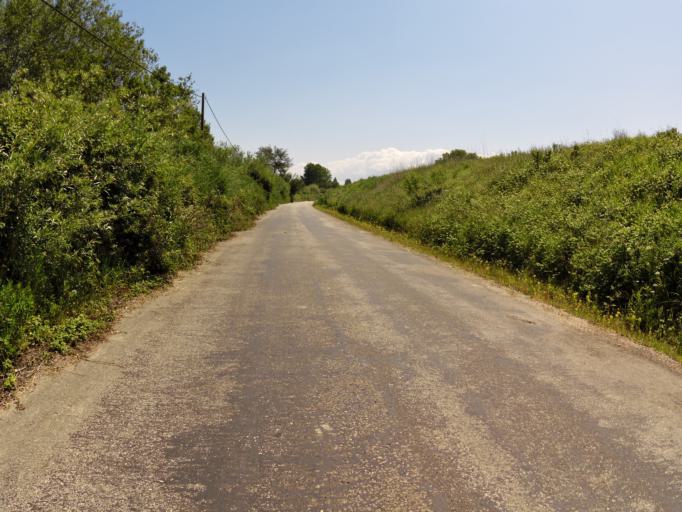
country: PT
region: Coimbra
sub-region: Montemor-O-Velho
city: Montemor-o-Velho
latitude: 40.1493
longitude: -8.7214
